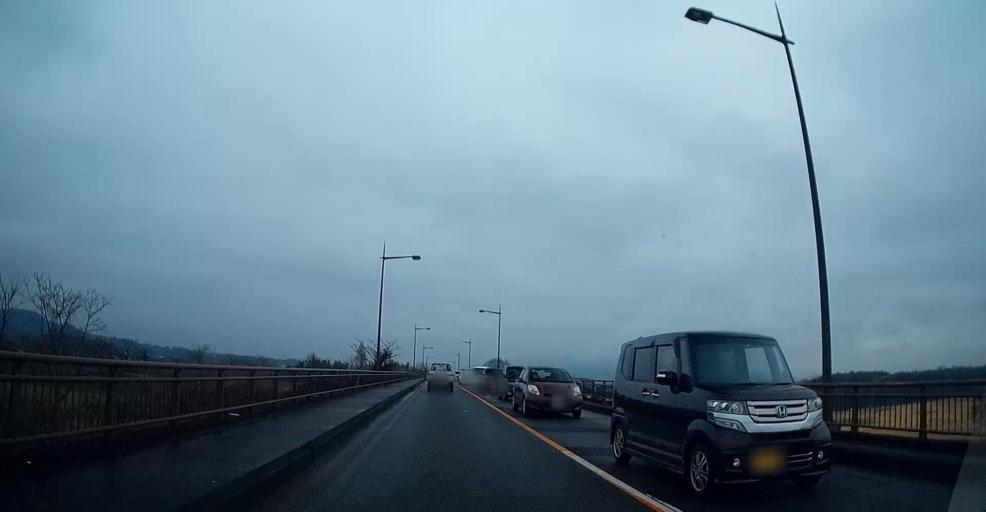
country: JP
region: Kumamoto
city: Kumamoto
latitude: 32.7368
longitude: 130.7398
